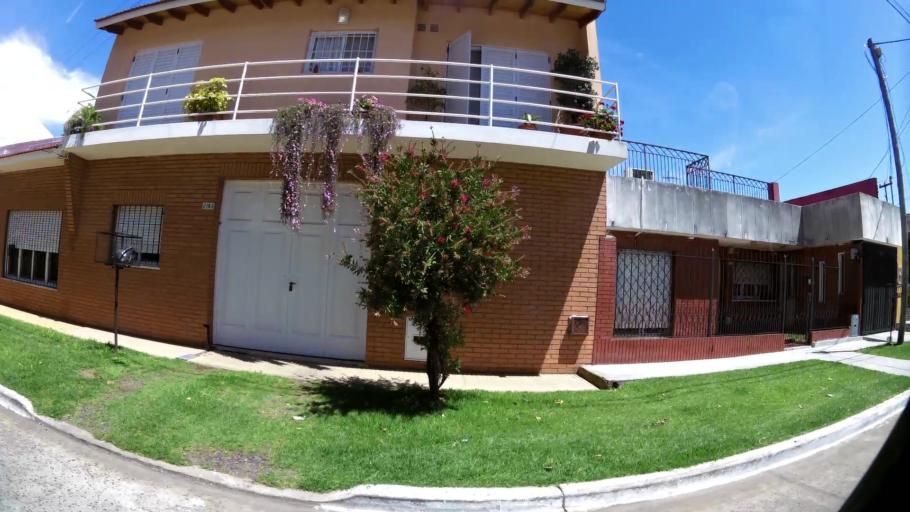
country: AR
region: Buenos Aires
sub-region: Partido de Quilmes
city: Quilmes
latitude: -34.7446
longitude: -58.2817
